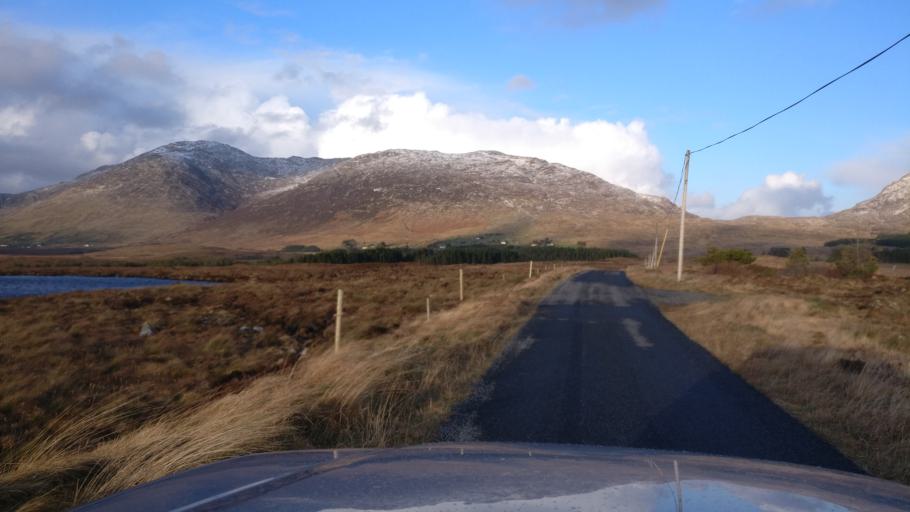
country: IE
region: Connaught
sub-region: County Galway
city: Clifden
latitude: 53.4740
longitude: -9.6897
